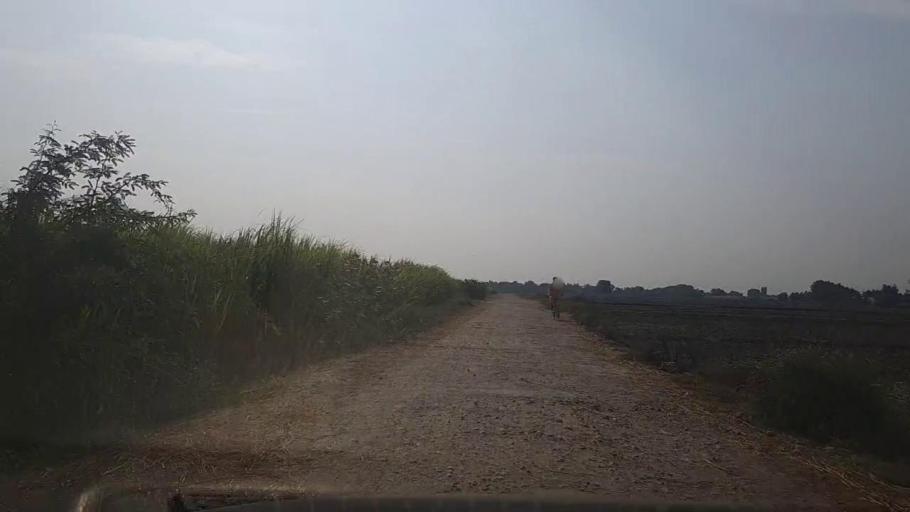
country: PK
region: Sindh
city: Bulri
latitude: 25.0115
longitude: 68.2998
